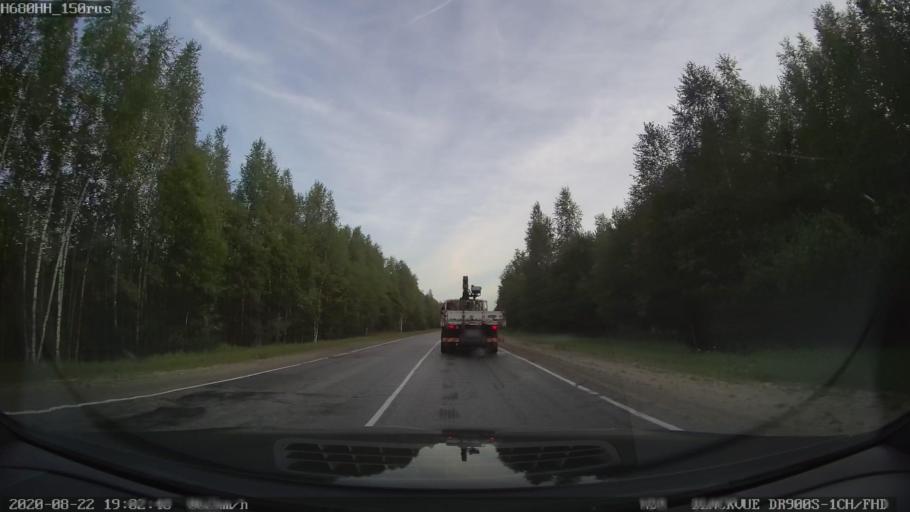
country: RU
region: Tverskaya
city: Sakharovo
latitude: 57.1051
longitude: 36.1205
